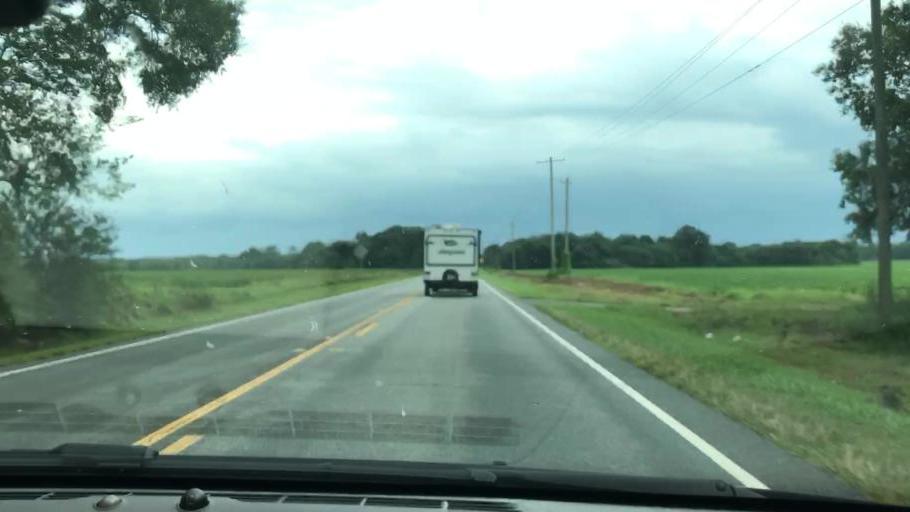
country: US
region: Georgia
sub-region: Early County
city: Blakely
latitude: 31.3901
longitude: -84.9522
